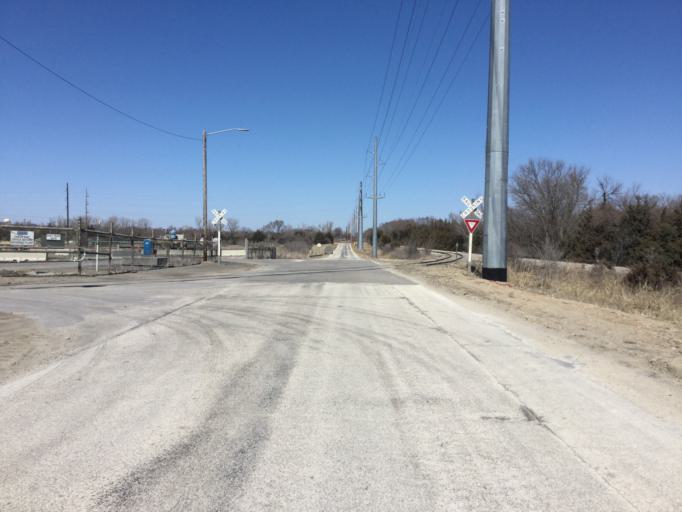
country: US
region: Kansas
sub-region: Allen County
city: Humboldt
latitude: 37.7967
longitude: -95.4291
